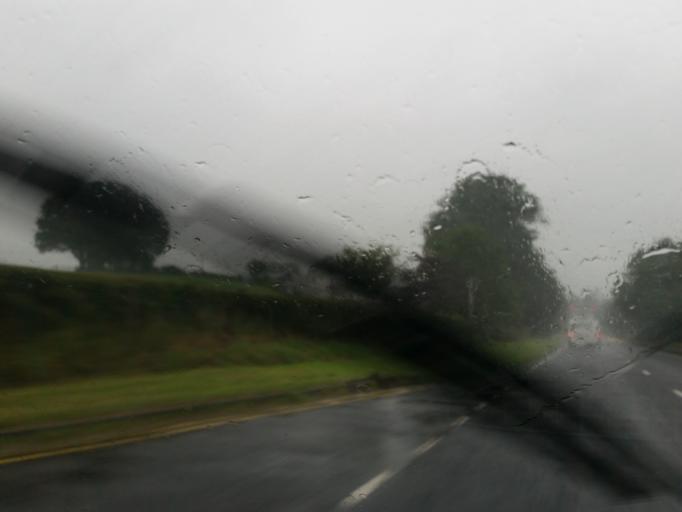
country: GB
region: Northern Ireland
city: Fivemiletown
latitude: 54.4214
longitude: -7.1460
